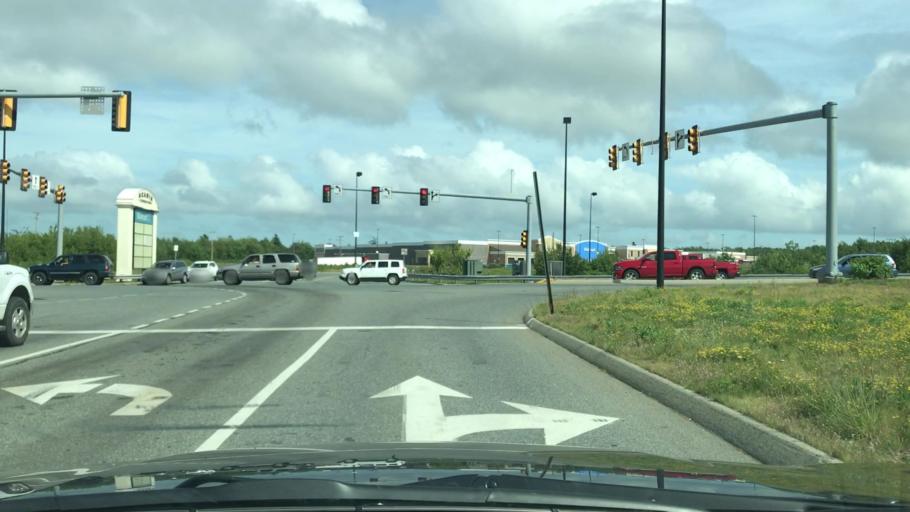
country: US
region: Maine
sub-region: Hancock County
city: Ellsworth
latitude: 44.5268
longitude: -68.3972
